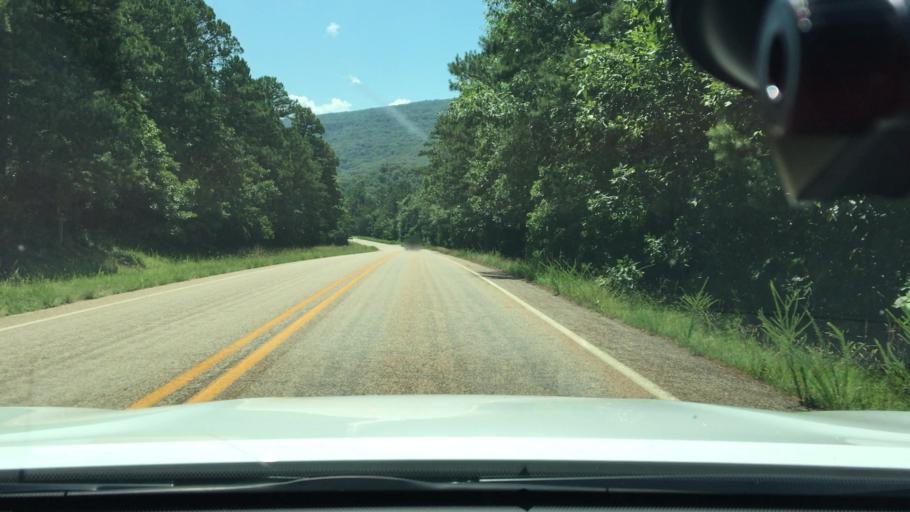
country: US
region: Arkansas
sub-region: Logan County
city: Paris
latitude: 35.1952
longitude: -93.6324
